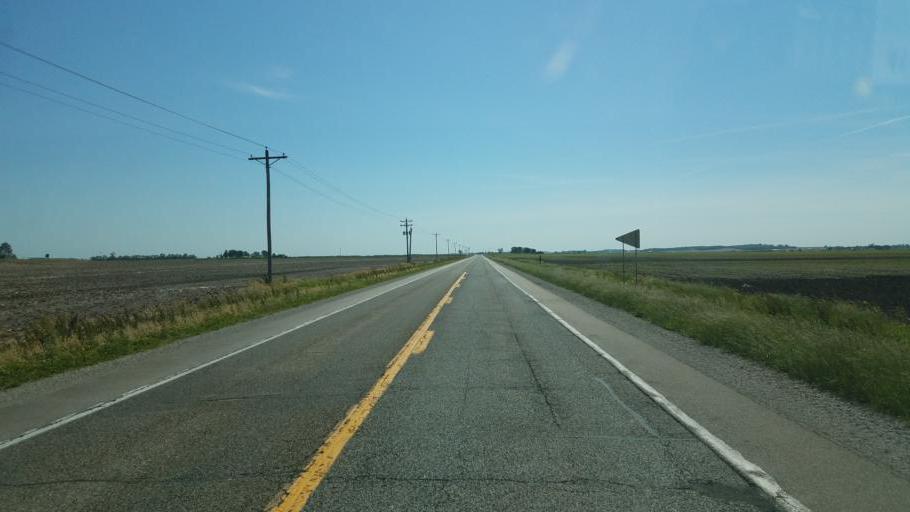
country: US
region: Illinois
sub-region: Mason County
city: Mason City
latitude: 40.3041
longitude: -89.7499
